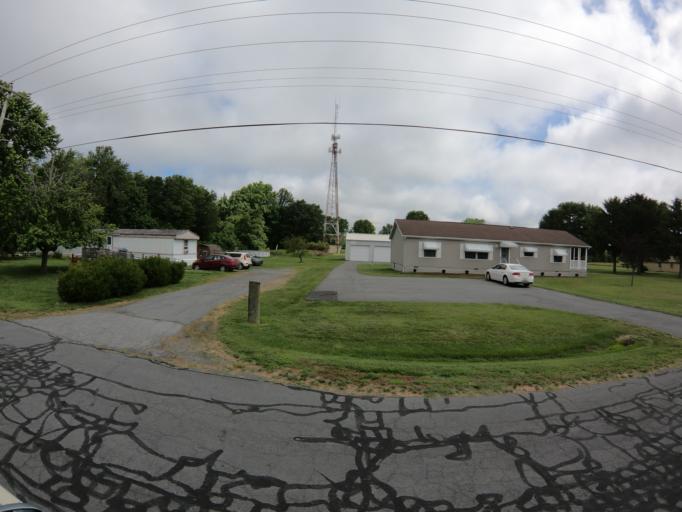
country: US
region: Delaware
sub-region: Kent County
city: Riverview
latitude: 39.0115
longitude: -75.5078
